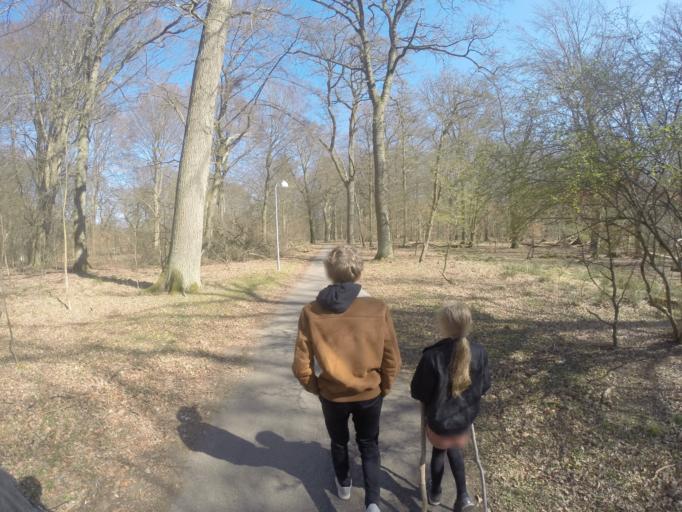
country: DK
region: Capital Region
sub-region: Rudersdal Kommune
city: Trorod
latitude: 55.8022
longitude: 12.5511
